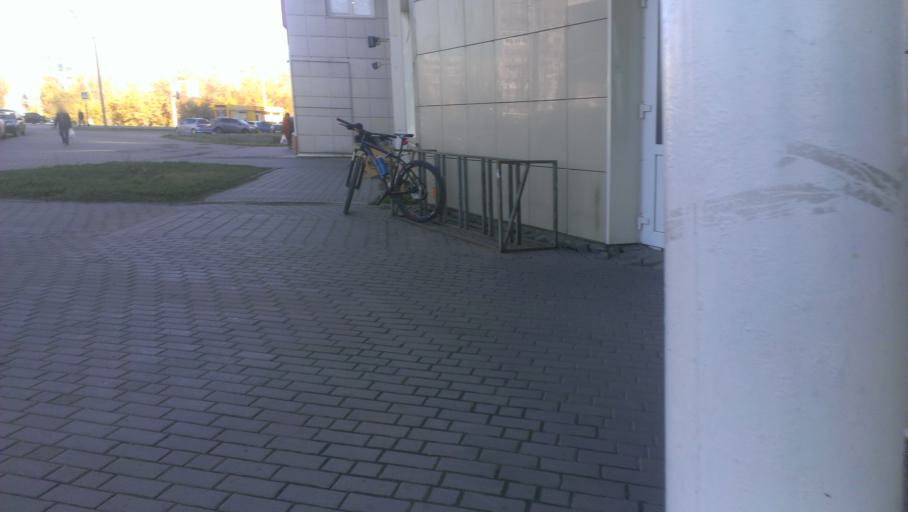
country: RU
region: Altai Krai
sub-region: Gorod Barnaulskiy
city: Barnaul
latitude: 53.3411
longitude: 83.6979
